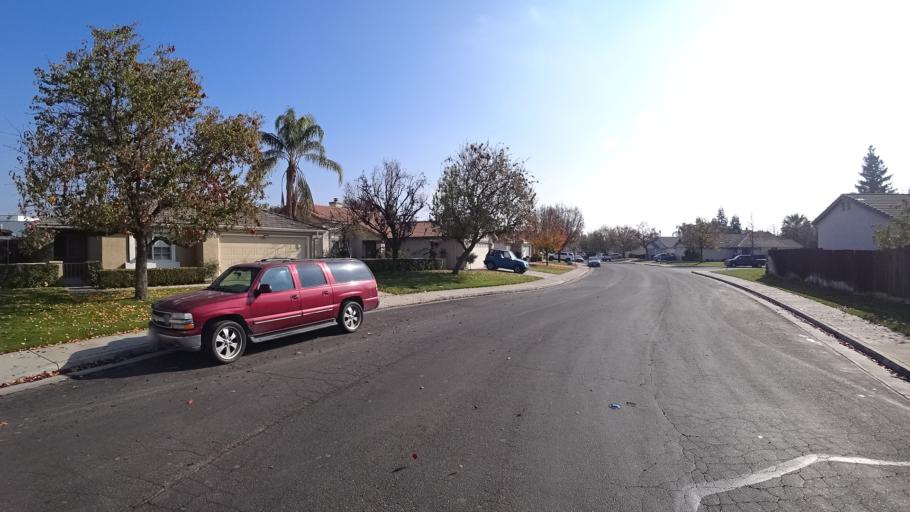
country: US
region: California
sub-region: Kern County
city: Greenacres
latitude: 35.3100
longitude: -119.0804
